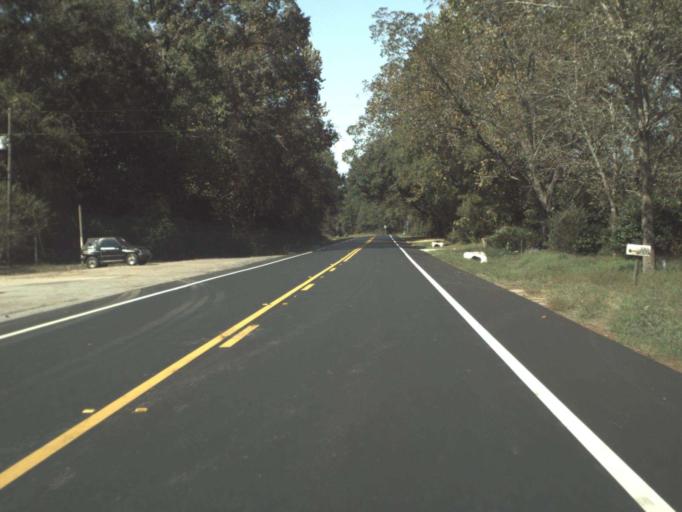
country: US
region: Florida
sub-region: Walton County
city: DeFuniak Springs
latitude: 30.8206
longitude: -86.2138
